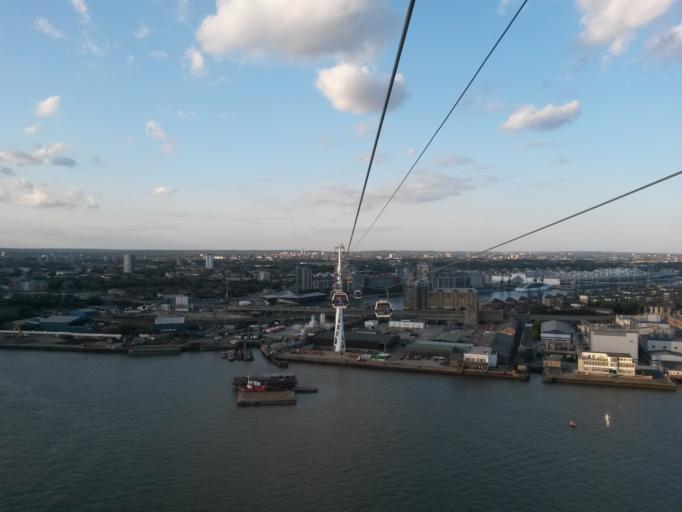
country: GB
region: England
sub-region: Greater London
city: Poplar
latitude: 51.5013
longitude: 0.0102
